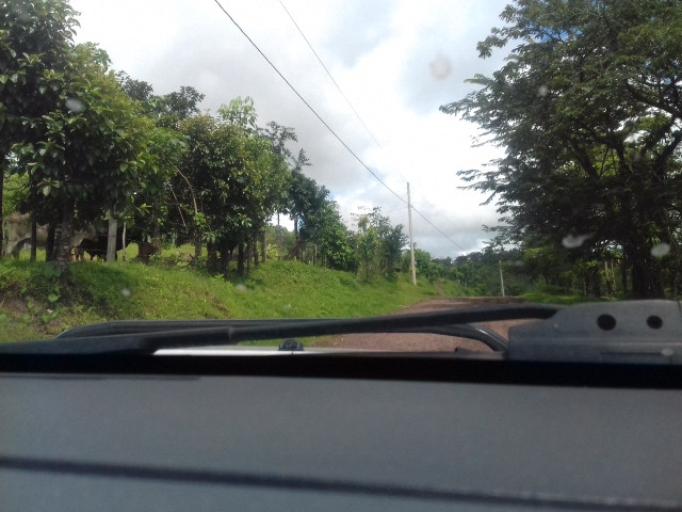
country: NI
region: Matagalpa
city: Rio Blanco
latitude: 12.9908
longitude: -85.1911
